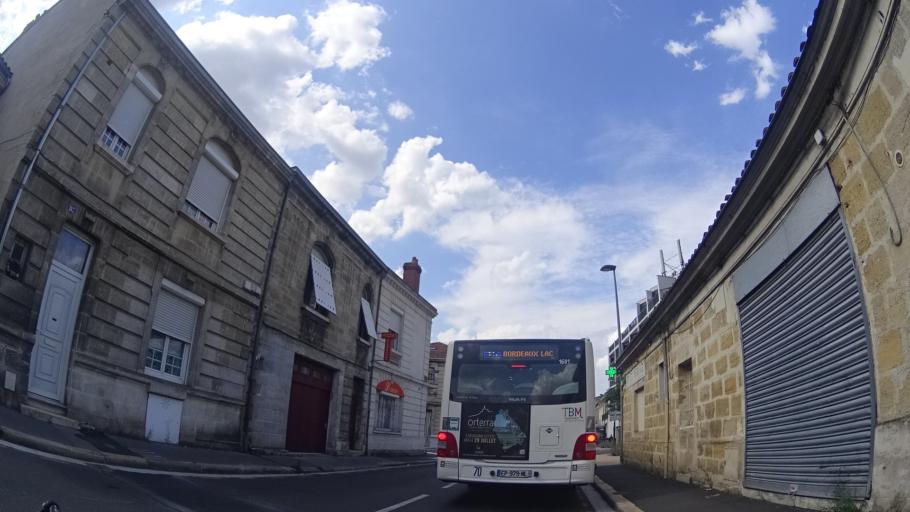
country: FR
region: Aquitaine
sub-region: Departement de la Gironde
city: Begles
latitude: 44.8215
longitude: -0.5658
